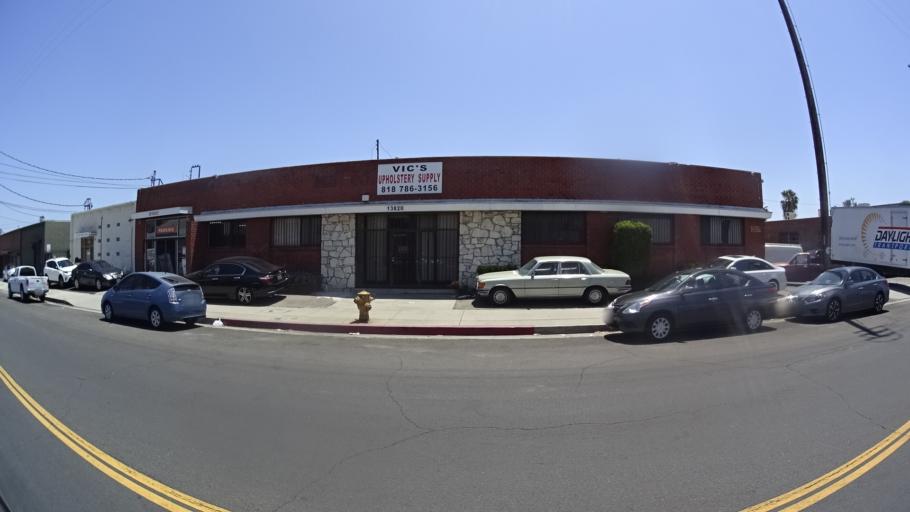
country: US
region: California
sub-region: Los Angeles County
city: Van Nuys
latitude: 34.2100
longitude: -118.4341
